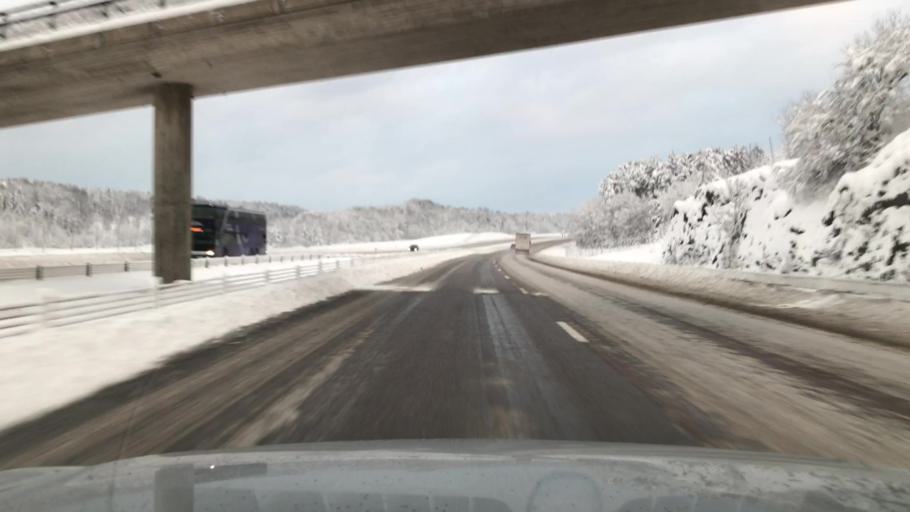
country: SE
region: Soedermanland
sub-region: Gnesta Kommun
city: Gnesta
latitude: 58.8897
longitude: 17.2627
